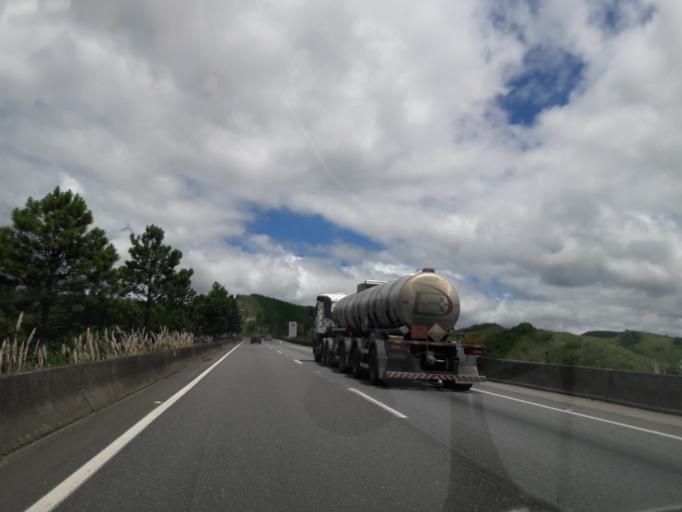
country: BR
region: Parana
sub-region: Campina Grande Do Sul
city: Campina Grande do Sul
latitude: -25.1015
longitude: -48.8299
